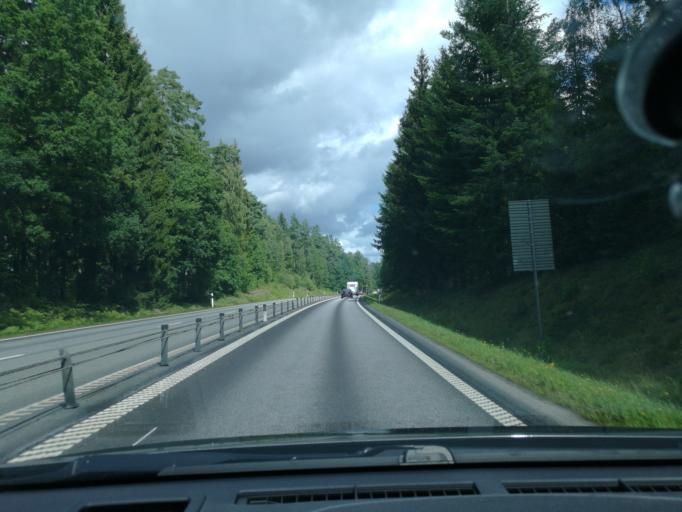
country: SE
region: Skane
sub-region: Osby Kommun
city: Osby
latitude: 56.3606
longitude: 14.0157
